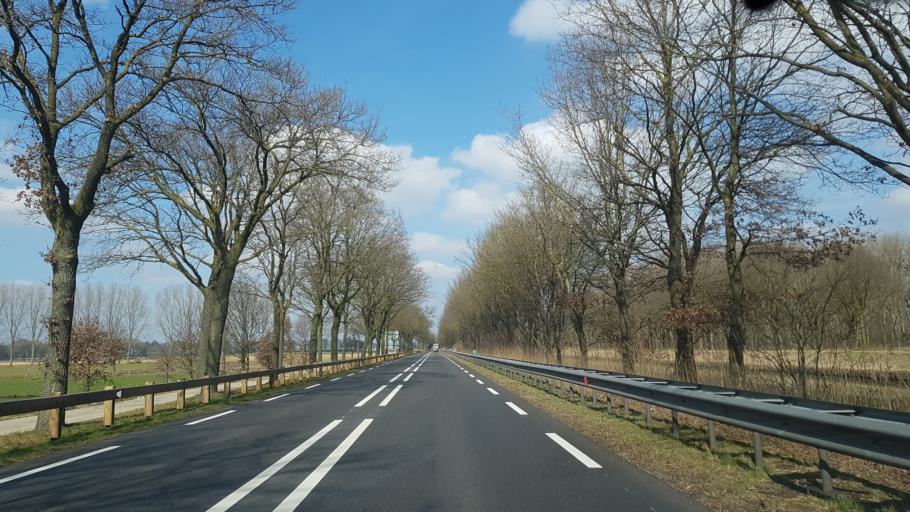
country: NL
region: North Brabant
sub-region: Gemeente Someren
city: Someren
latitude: 51.3665
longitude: 5.7403
